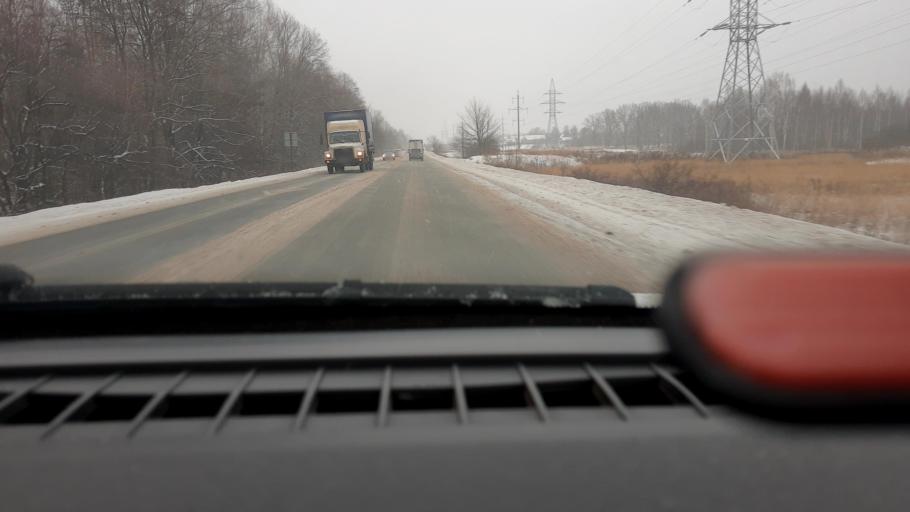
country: RU
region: Nizjnij Novgorod
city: Lukino
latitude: 56.4570
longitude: 43.6256
